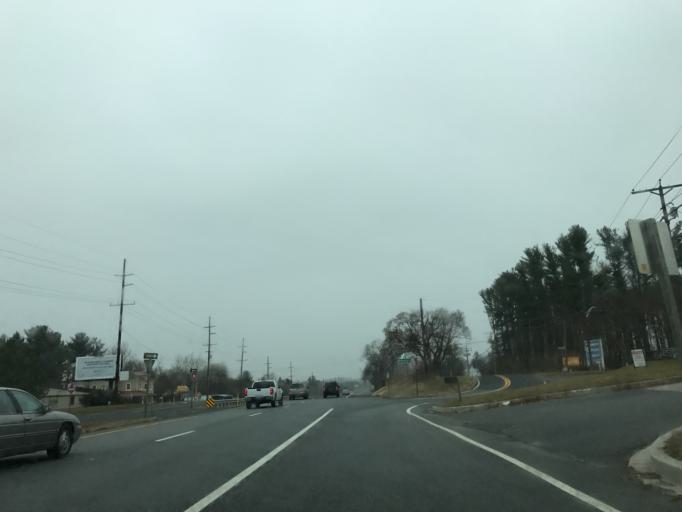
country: US
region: Maryland
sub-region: Baltimore County
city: Reisterstown
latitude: 39.4994
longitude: -76.8946
